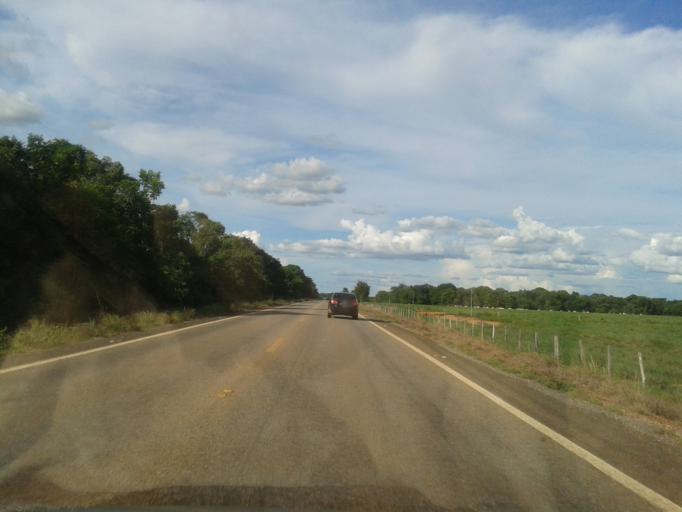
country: BR
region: Goias
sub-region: Mozarlandia
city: Mozarlandia
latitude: -14.3201
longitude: -50.4097
